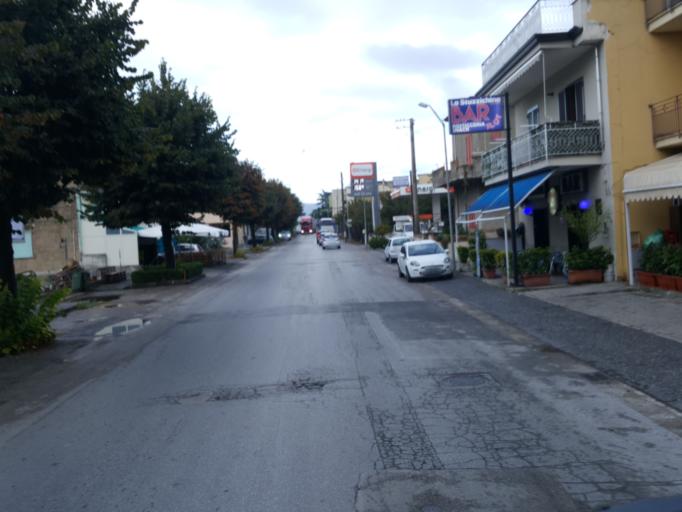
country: IT
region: Campania
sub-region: Provincia di Napoli
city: Palma Campania
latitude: 40.8784
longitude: 14.5510
